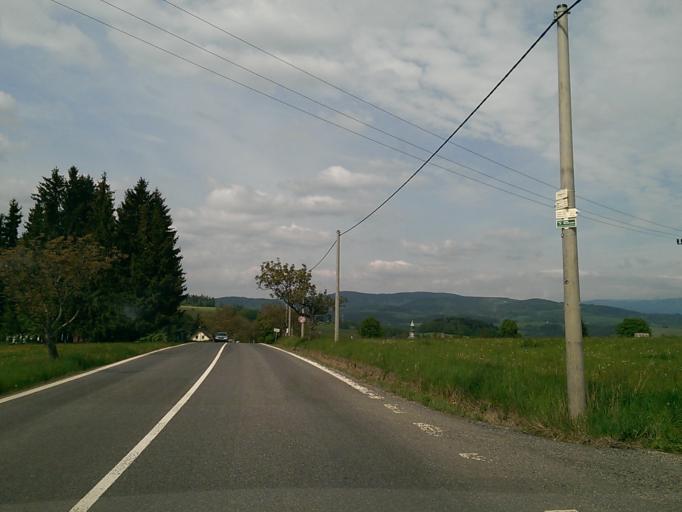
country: CZ
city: Plavy
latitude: 50.6846
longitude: 15.2978
